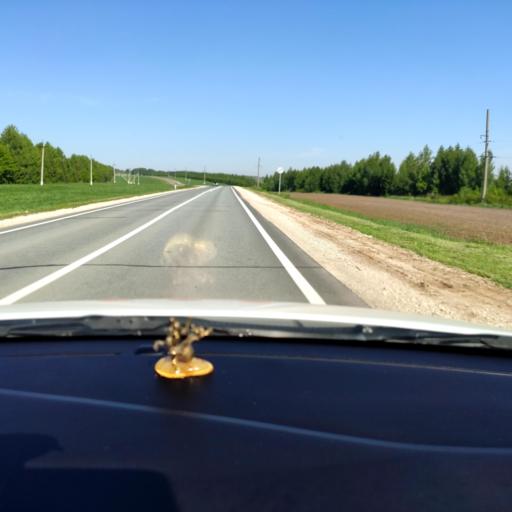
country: RU
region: Tatarstan
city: Vysokaya Gora
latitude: 56.0257
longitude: 49.2547
